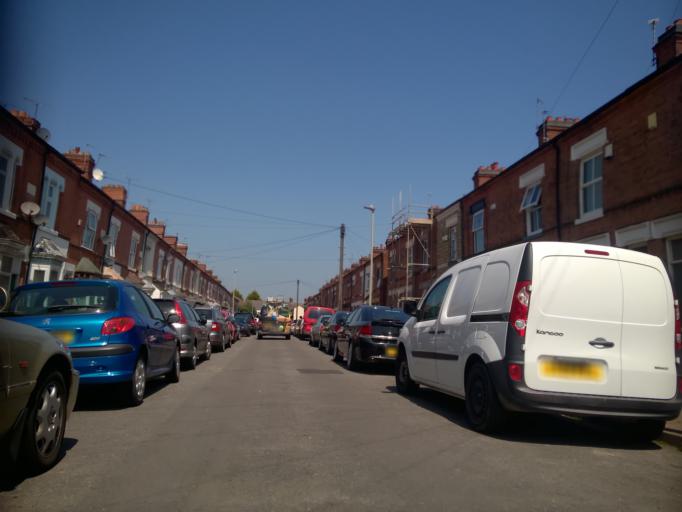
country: GB
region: England
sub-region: City of Leicester
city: Leicester
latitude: 52.6400
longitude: -1.1543
